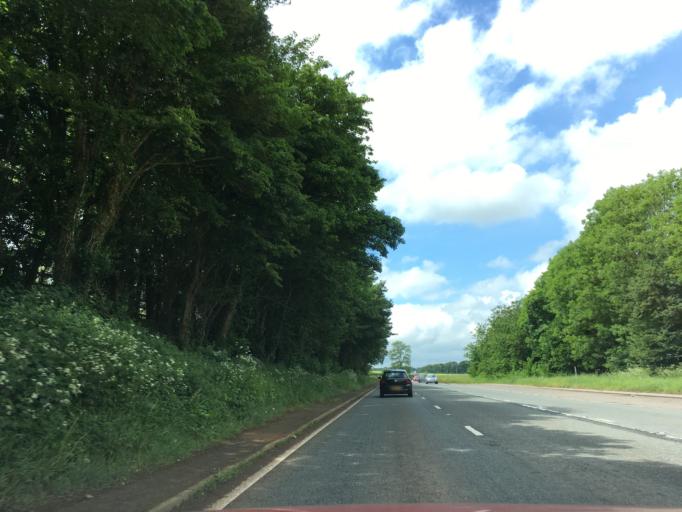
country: GB
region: England
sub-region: Devon
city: Uffculme
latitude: 50.9658
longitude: -3.2574
